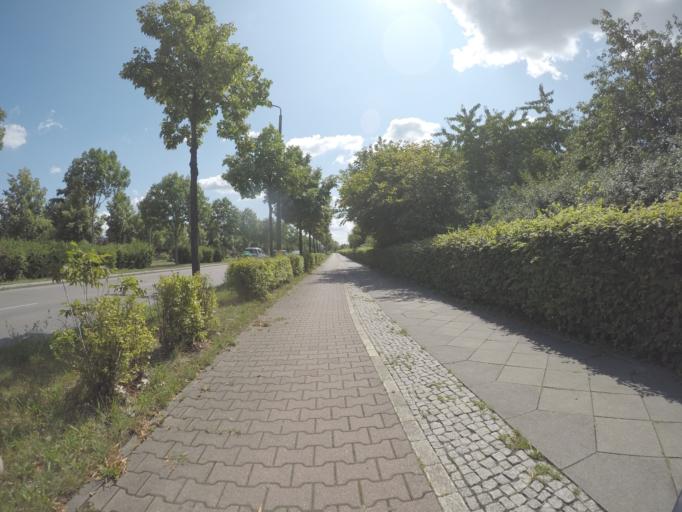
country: DE
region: Berlin
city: Marzahn
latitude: 52.5333
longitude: 13.5658
